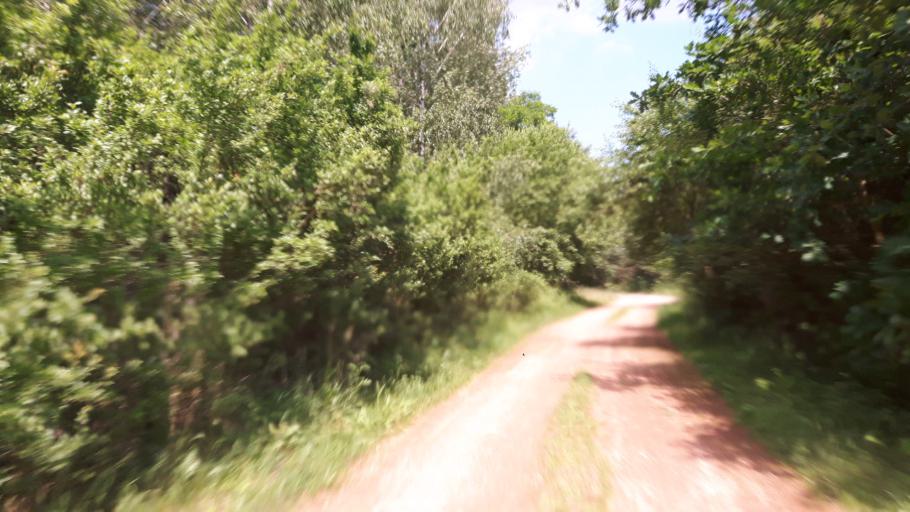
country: DE
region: Saxony-Anhalt
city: Radis
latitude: 51.7537
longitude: 12.4836
